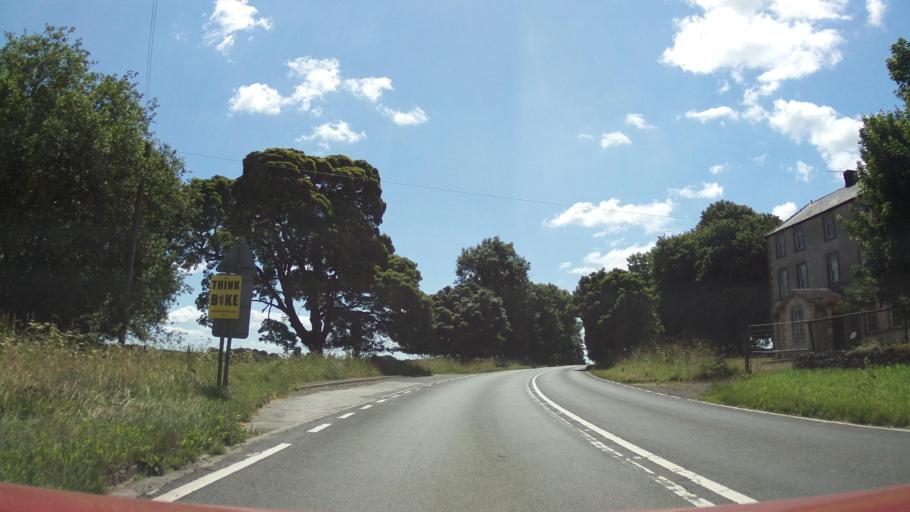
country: GB
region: England
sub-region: Derbyshire
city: Bakewell
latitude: 53.1381
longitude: -1.7529
